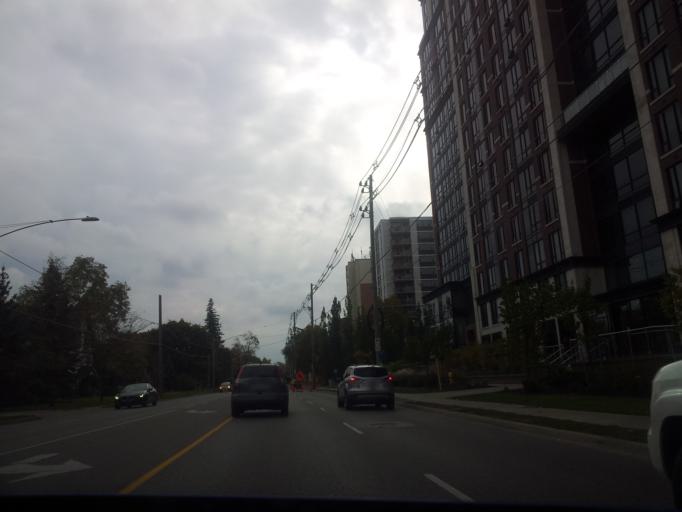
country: CA
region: Ontario
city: London
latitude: 43.0132
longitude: -81.2657
